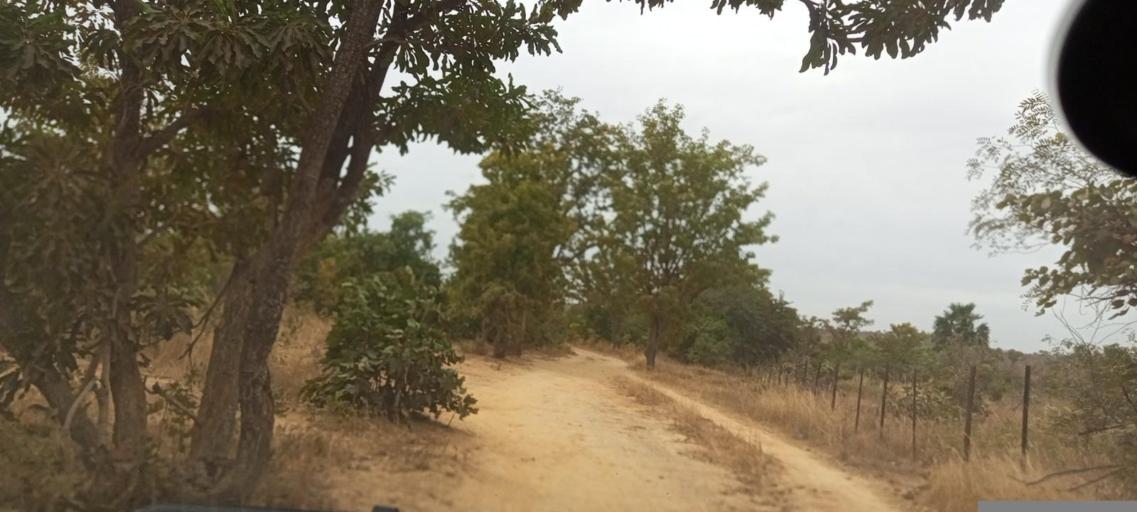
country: ML
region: Koulikoro
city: Kati
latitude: 12.7700
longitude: -8.3732
